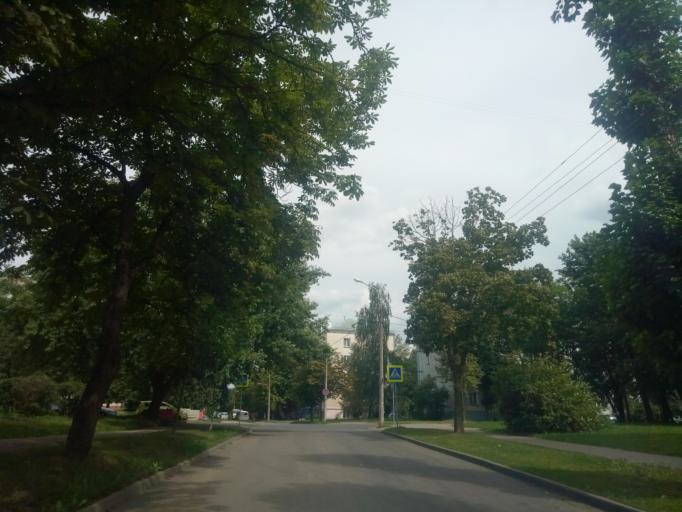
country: BY
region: Minsk
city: Minsk
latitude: 53.8965
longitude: 27.5187
